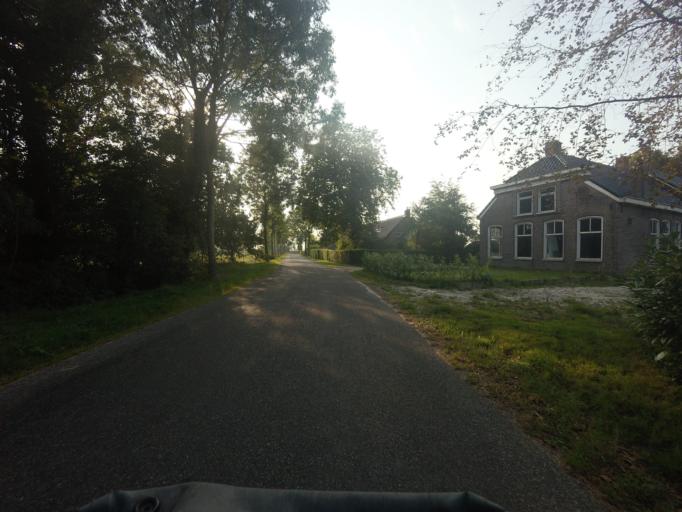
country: NL
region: Drenthe
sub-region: Gemeente Tynaarlo
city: Vries
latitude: 53.1179
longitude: 6.5329
